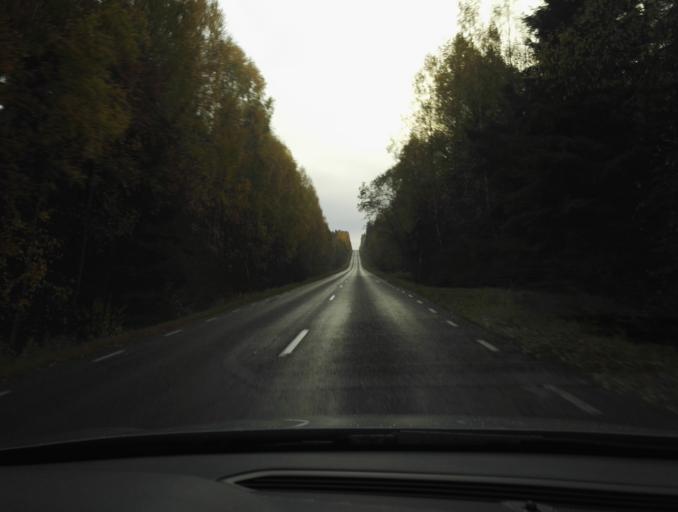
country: SE
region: Kronoberg
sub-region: Alvesta Kommun
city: Moheda
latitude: 57.0108
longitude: 14.7082
